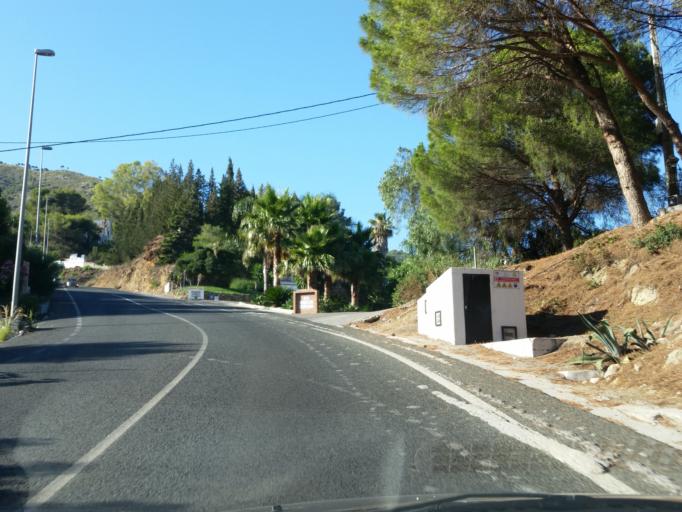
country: ES
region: Andalusia
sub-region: Provincia de Malaga
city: Mijas
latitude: 36.5960
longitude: -4.6320
